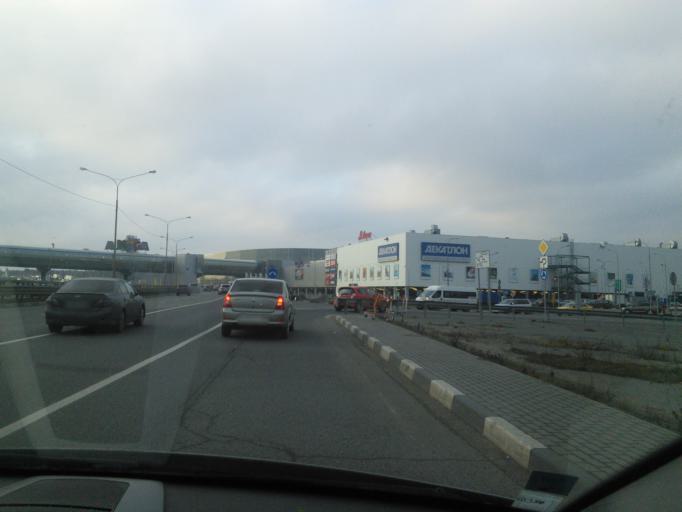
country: RU
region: Moskovskaya
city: Kotel'niki
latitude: 55.6555
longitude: 37.8496
